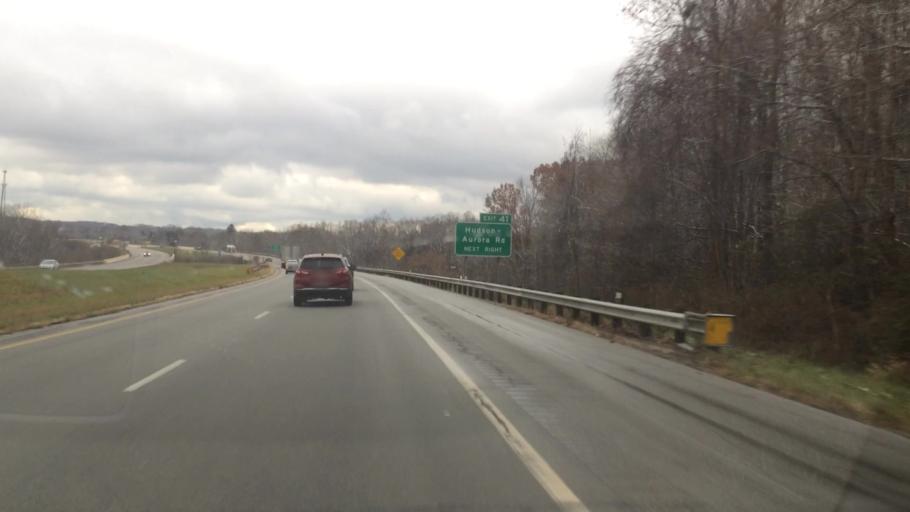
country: US
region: Ohio
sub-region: Summit County
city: Hudson
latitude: 41.2666
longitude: -81.3958
